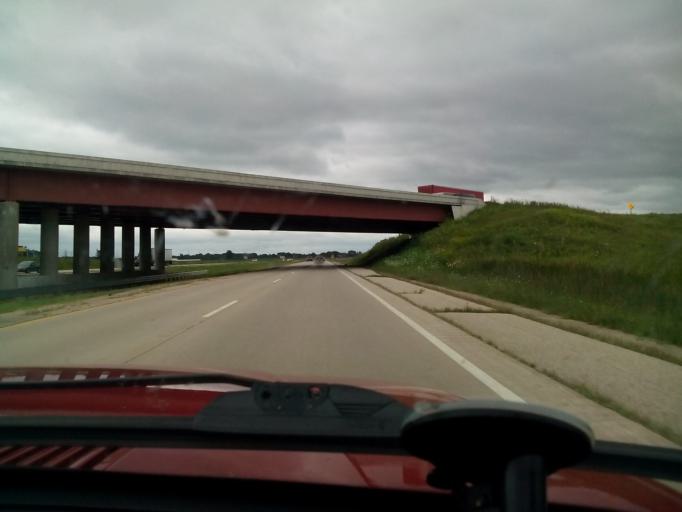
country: US
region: Wisconsin
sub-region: Columbia County
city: Columbus
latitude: 43.3178
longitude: -89.0457
